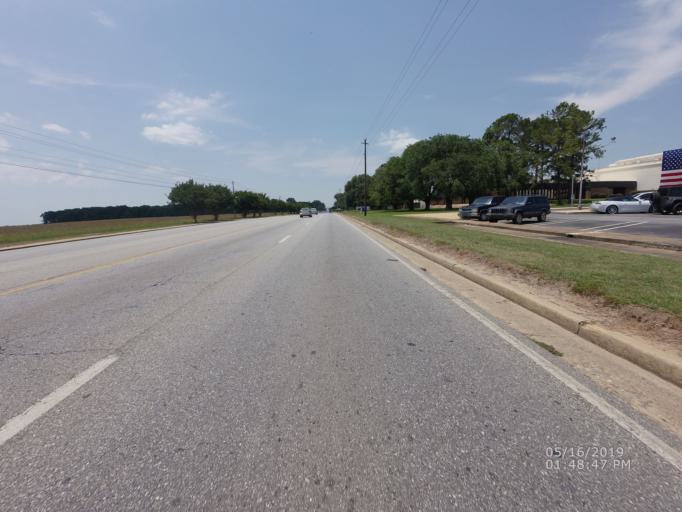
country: US
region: Georgia
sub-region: Dougherty County
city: Albany
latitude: 31.5491
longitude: -84.1805
